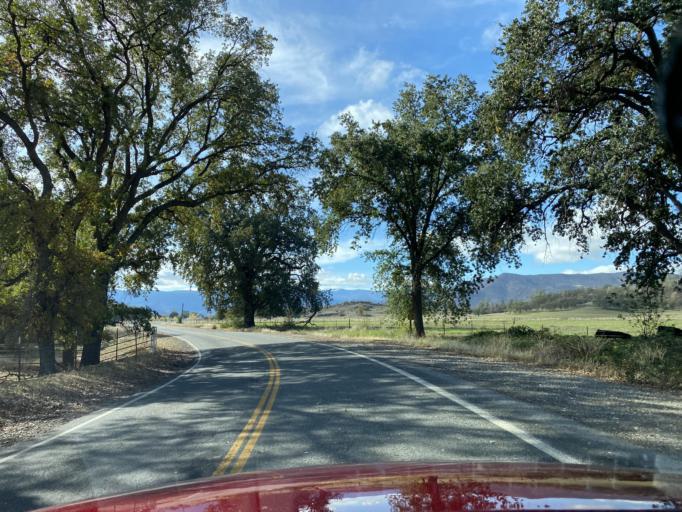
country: US
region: California
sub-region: Glenn County
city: Willows
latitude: 39.4135
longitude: -122.5443
